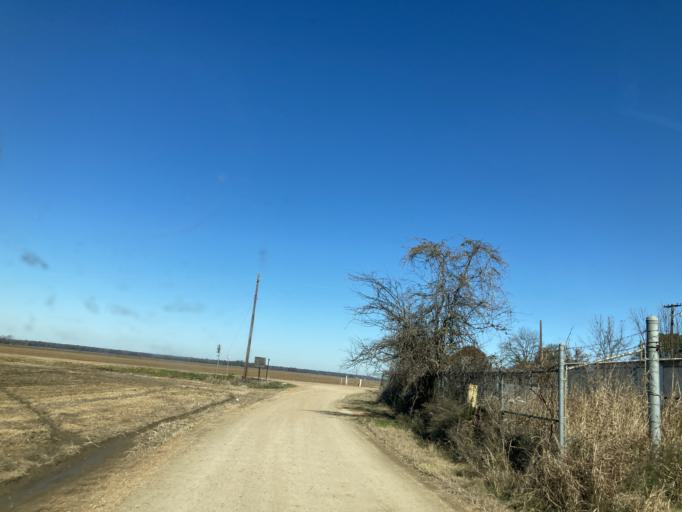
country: US
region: Mississippi
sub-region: Sharkey County
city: Rolling Fork
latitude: 32.8209
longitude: -90.7117
